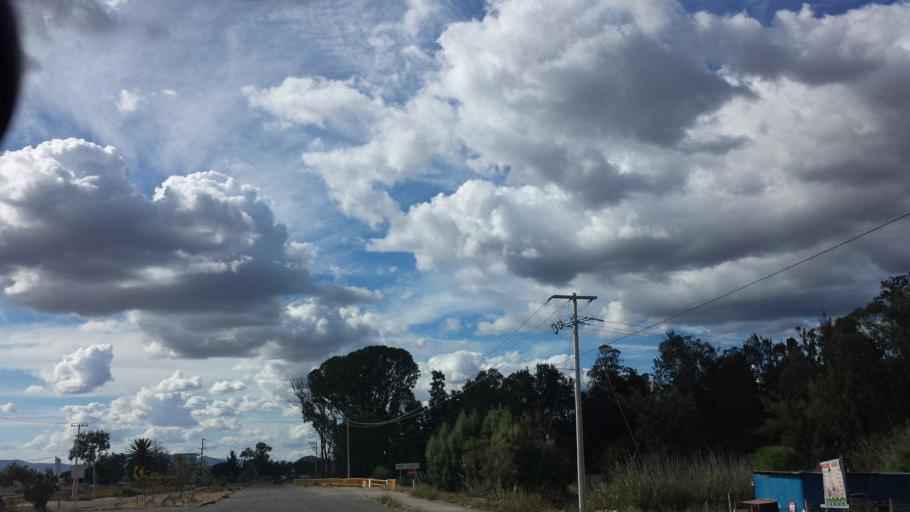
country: MX
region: Oaxaca
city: Tlacolula de Matamoros
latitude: 16.9507
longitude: -96.4650
